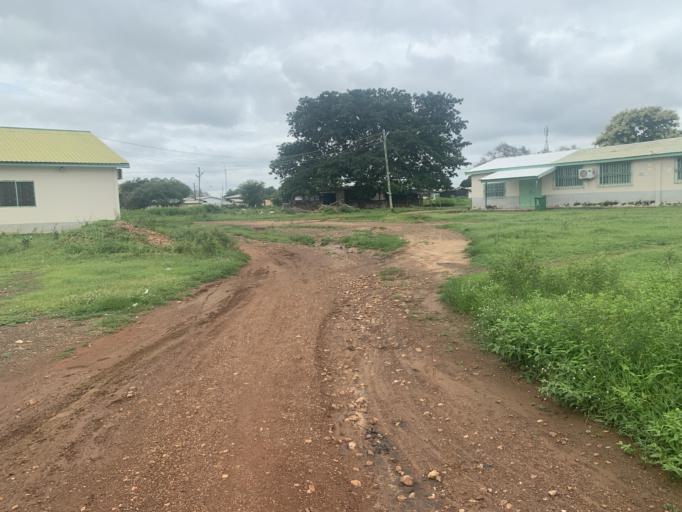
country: GH
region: Upper East
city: Navrongo
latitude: 10.8659
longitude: -1.0797
